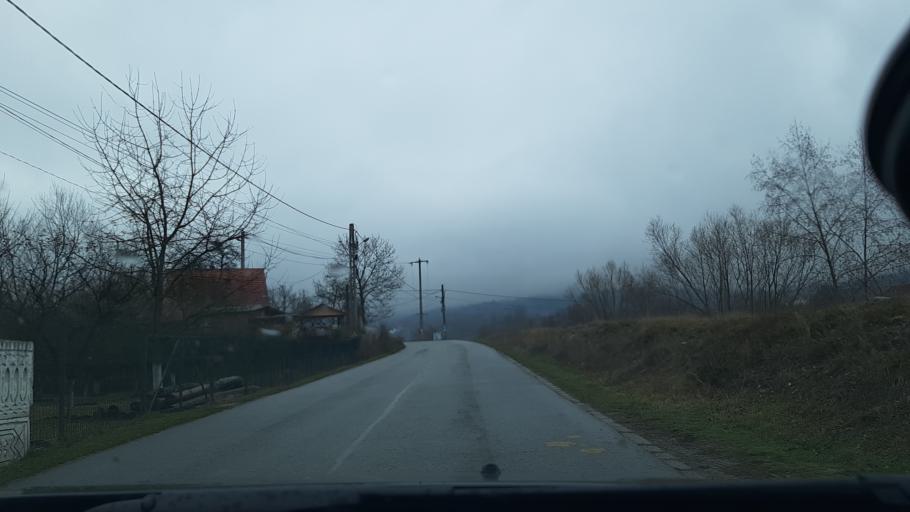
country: RO
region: Hunedoara
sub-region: Oras Petrila
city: Petrila
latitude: 45.4261
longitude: 23.4235
